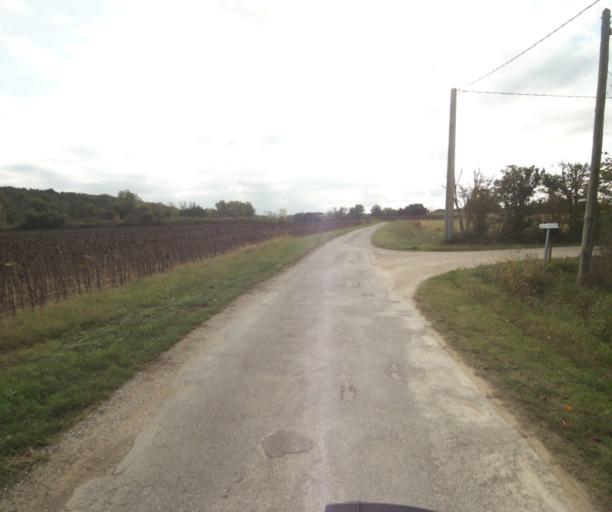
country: FR
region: Midi-Pyrenees
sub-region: Departement du Tarn-et-Garonne
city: Verdun-sur-Garonne
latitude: 43.8481
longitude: 1.1621
